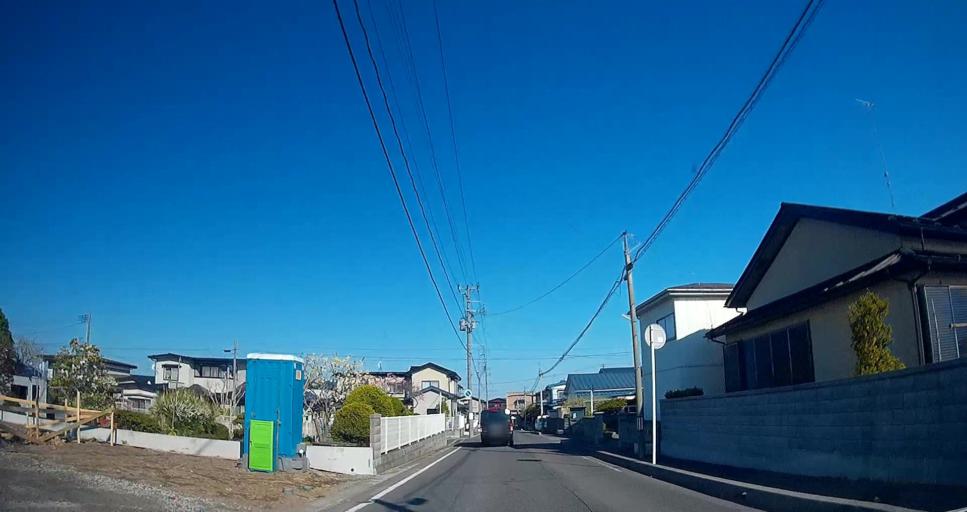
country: JP
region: Aomori
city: Hachinohe
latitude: 40.5250
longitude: 141.5504
